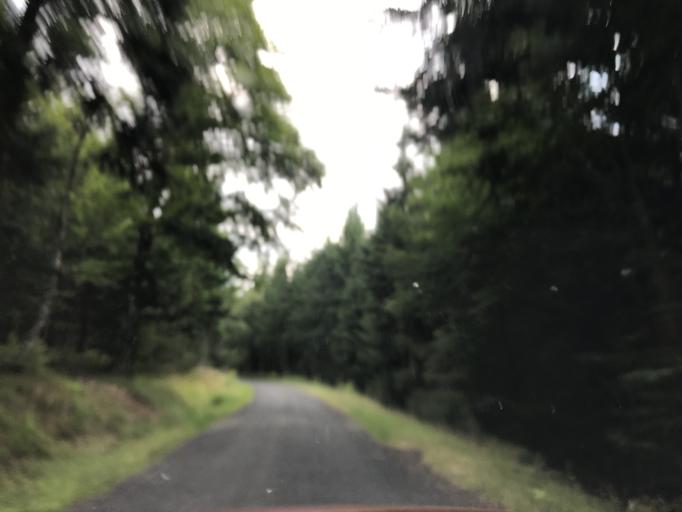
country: FR
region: Rhone-Alpes
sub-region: Departement de la Loire
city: Noiretable
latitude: 45.7633
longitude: 3.7279
